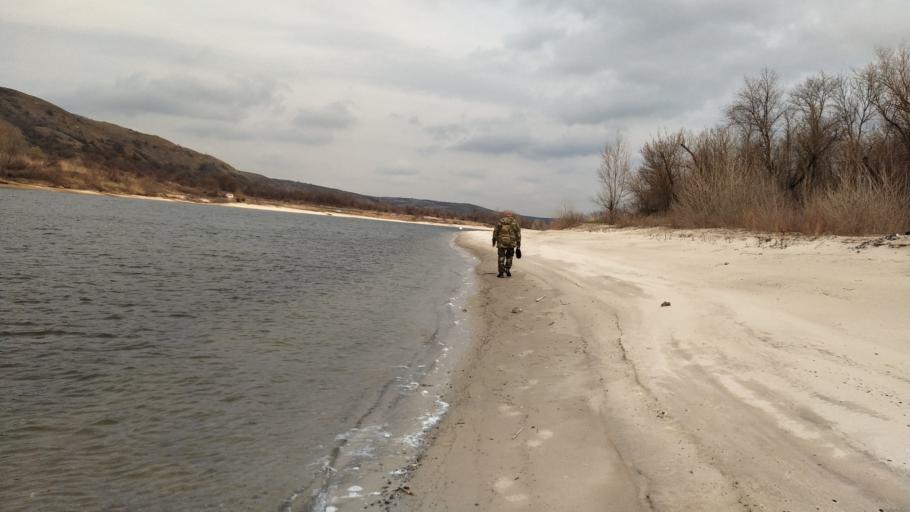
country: RU
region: Rostov
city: Semikarakorsk
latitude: 47.5593
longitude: 40.6732
